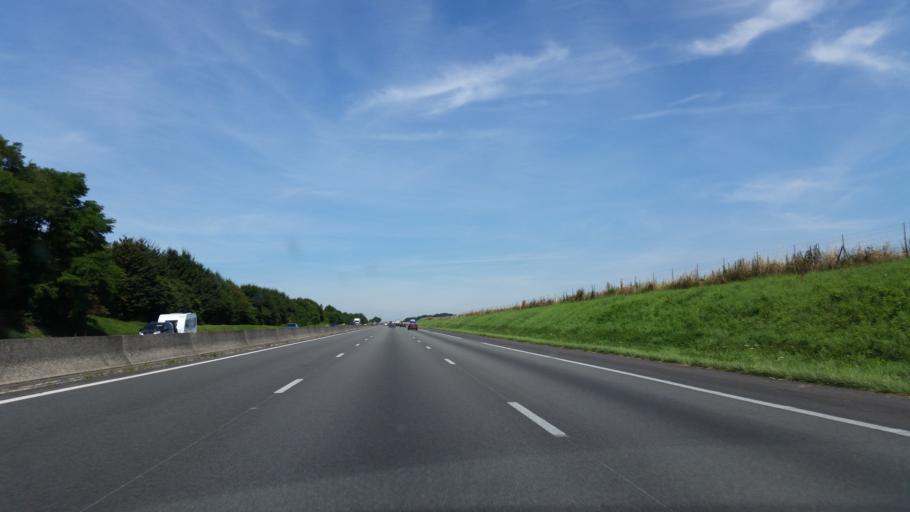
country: FR
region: Picardie
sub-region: Departement de la Somme
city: Peronne
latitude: 49.9213
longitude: 2.8514
